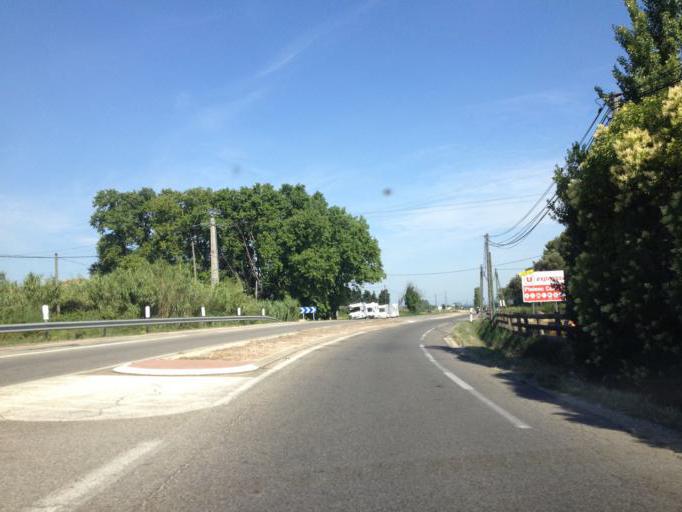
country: FR
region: Provence-Alpes-Cote d'Azur
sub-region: Departement du Vaucluse
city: Piolenc
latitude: 44.1650
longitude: 4.7678
